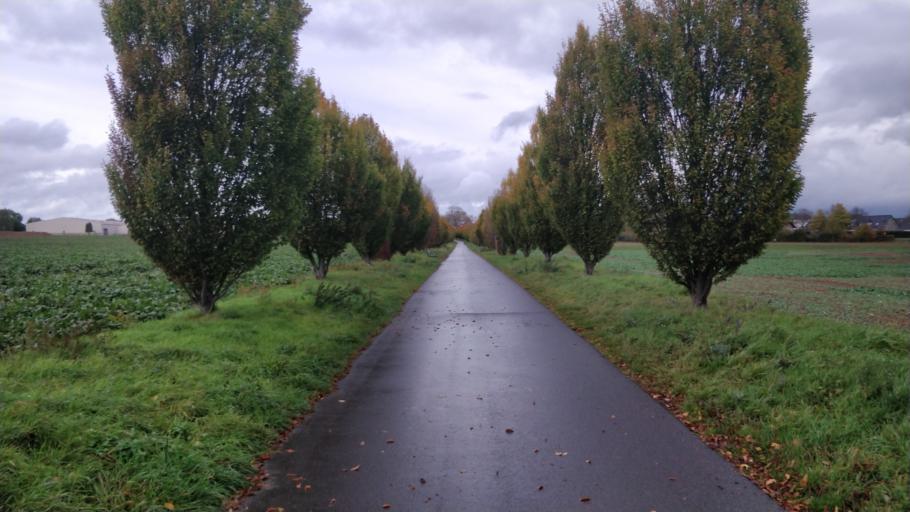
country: DE
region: North Rhine-Westphalia
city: Zulpich
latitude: 50.6846
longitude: 6.6585
